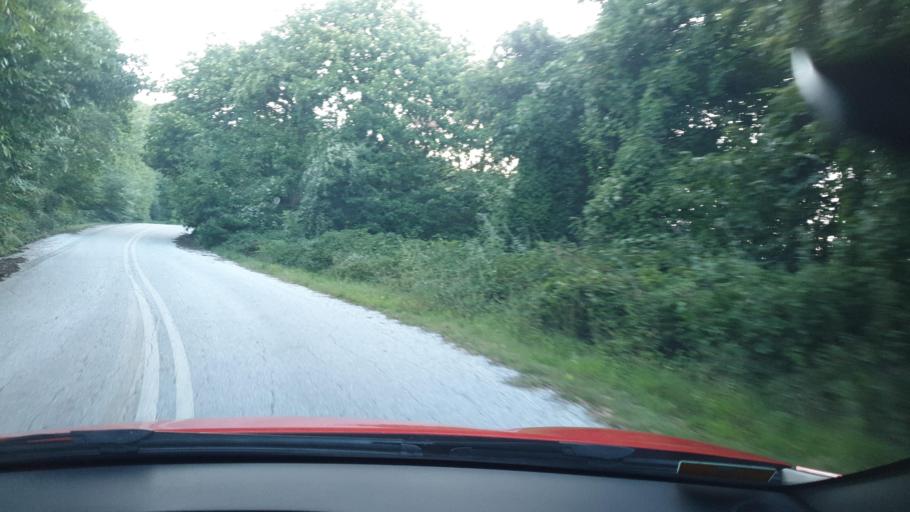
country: GR
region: Central Macedonia
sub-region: Nomos Chalkidikis
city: Galatista
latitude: 40.5079
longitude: 23.2603
